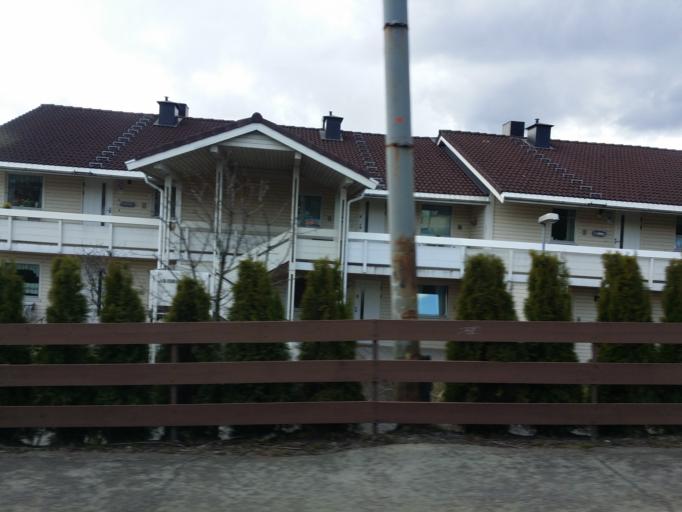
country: NO
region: Oslo
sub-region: Oslo
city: Oslo
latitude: 59.9472
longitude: 10.7897
